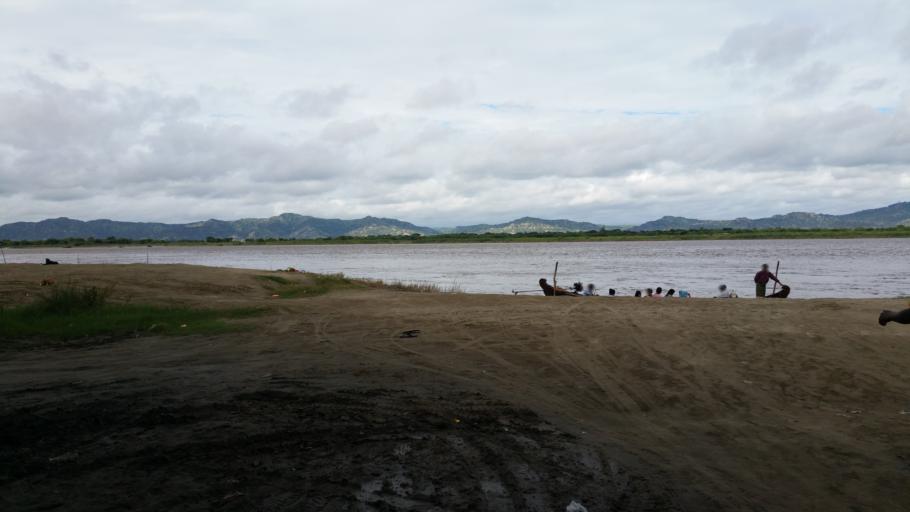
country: MM
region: Magway
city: Chauk
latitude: 21.1288
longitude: 94.8518
